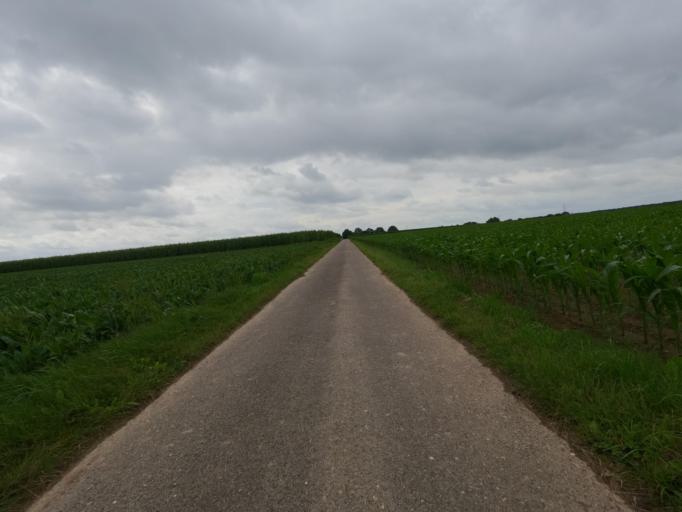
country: NL
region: Limburg
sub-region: Gemeente Echt-Susteren
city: Koningsbosch
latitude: 51.0259
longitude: 5.9568
